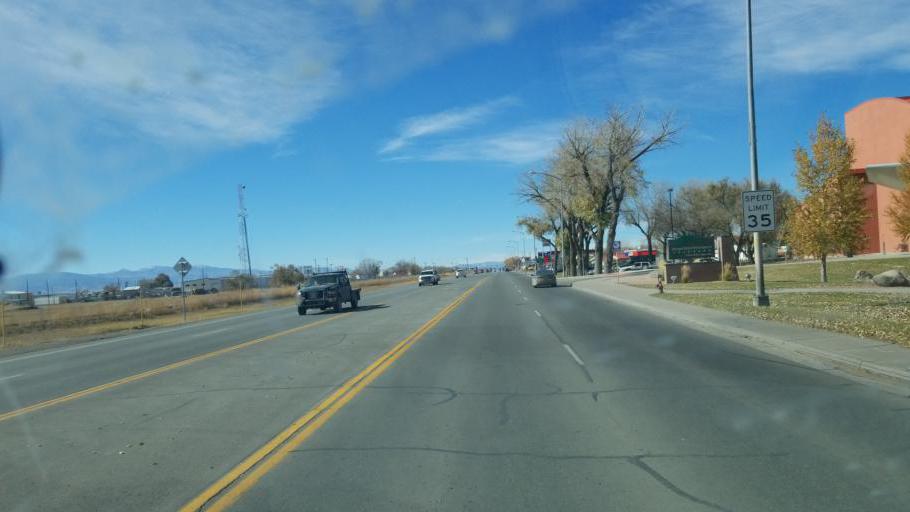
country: US
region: Colorado
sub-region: Alamosa County
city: Alamosa
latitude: 37.4687
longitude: -105.8790
